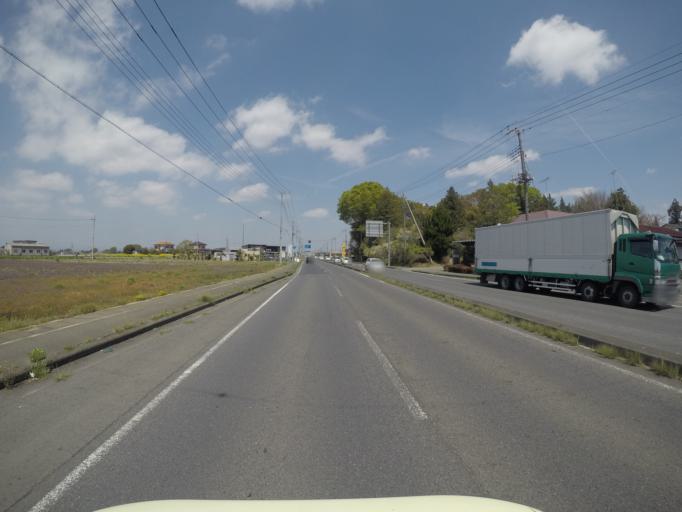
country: JP
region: Tochigi
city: Mibu
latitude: 36.4216
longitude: 139.7945
